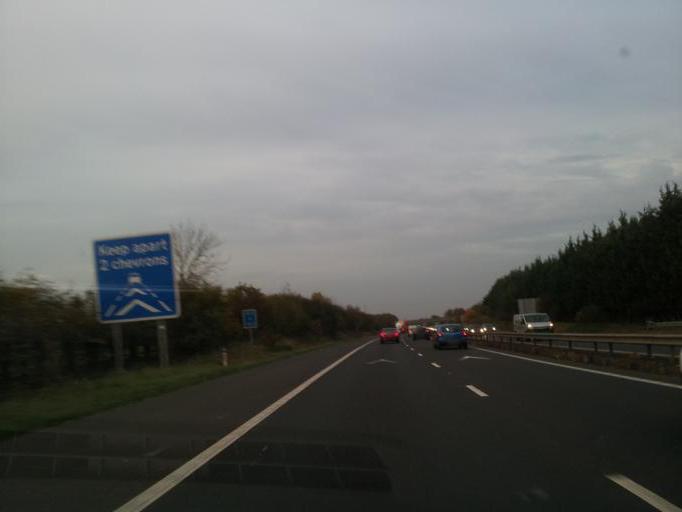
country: GB
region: England
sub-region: Cambridgeshire
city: Duxford
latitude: 52.1118
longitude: 0.1279
